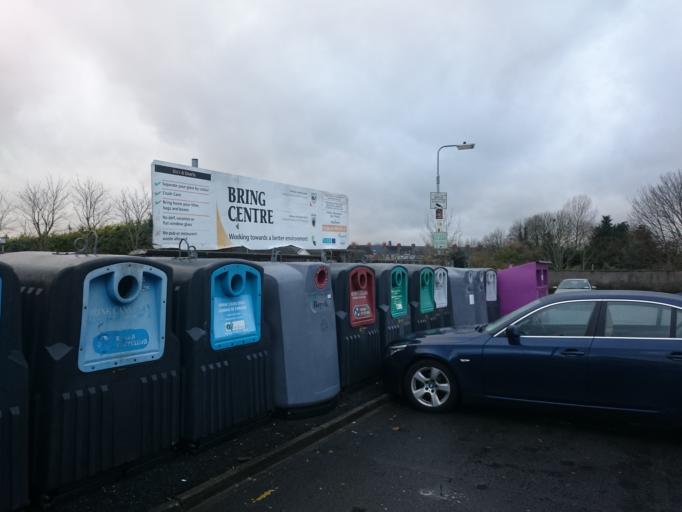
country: IE
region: Leinster
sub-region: Kilkenny
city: Kilkenny
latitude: 52.6552
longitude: -7.2482
